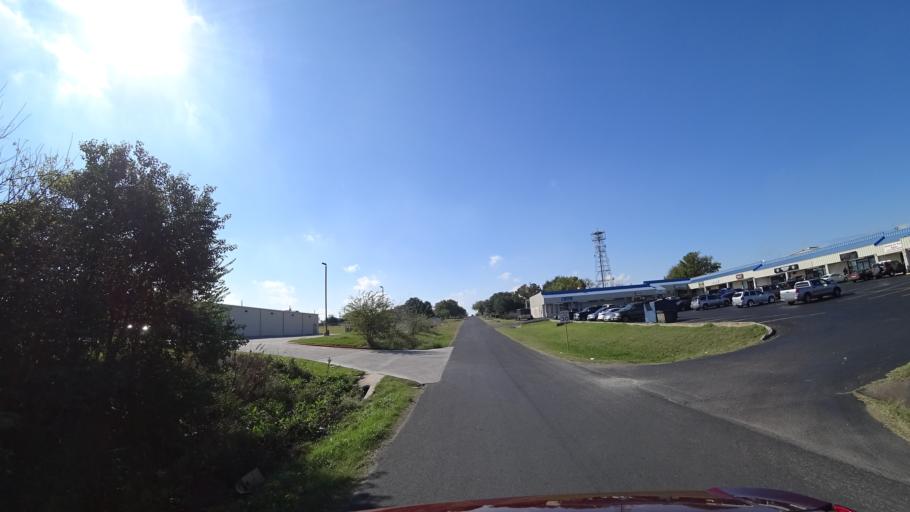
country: US
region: Texas
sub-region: Travis County
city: Windemere
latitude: 30.4459
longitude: -97.6508
